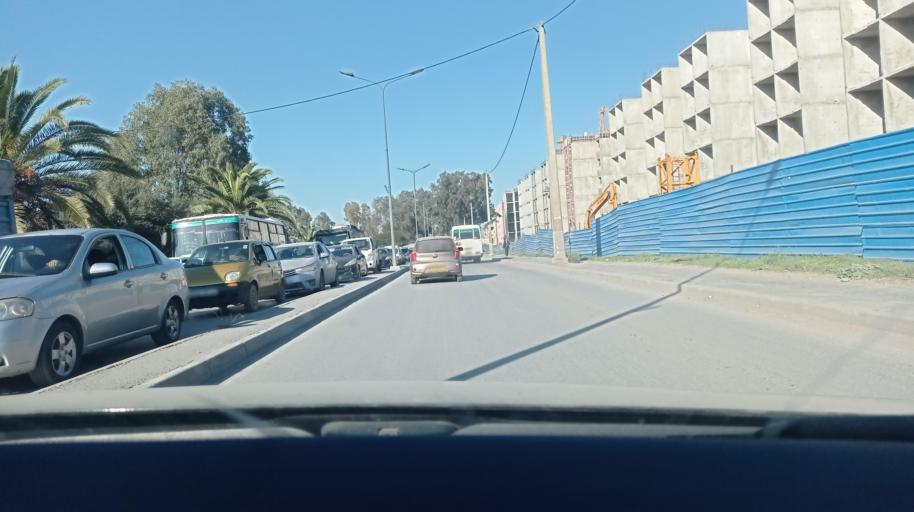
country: DZ
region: Tipaza
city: Baraki
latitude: 36.6566
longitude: 3.0856
